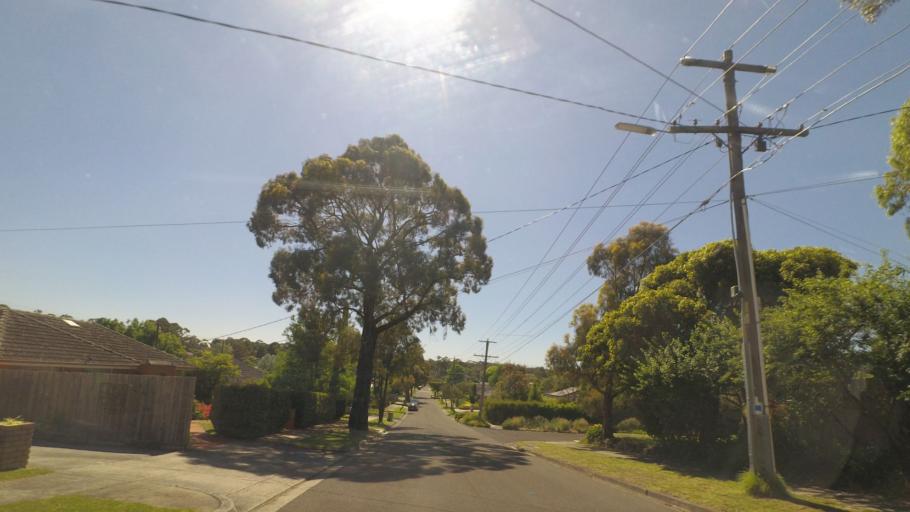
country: AU
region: Victoria
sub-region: Yarra Ranges
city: Kilsyth
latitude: -37.7977
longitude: 145.3159
